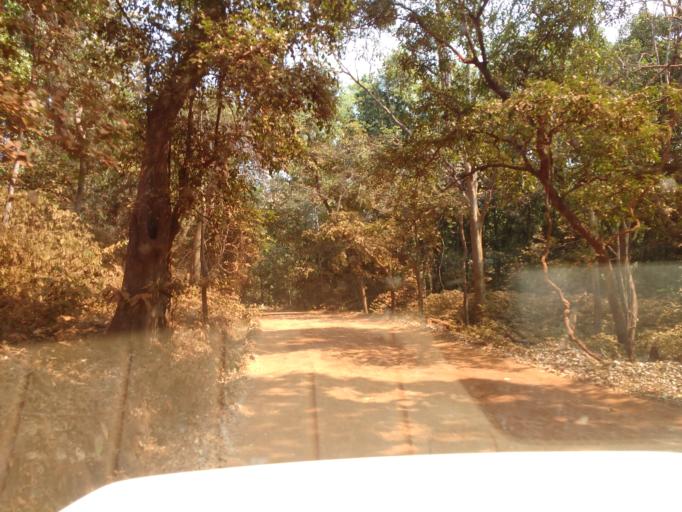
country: IN
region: Goa
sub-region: South Goa
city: Sanguem
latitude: 15.3402
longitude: 74.2630
